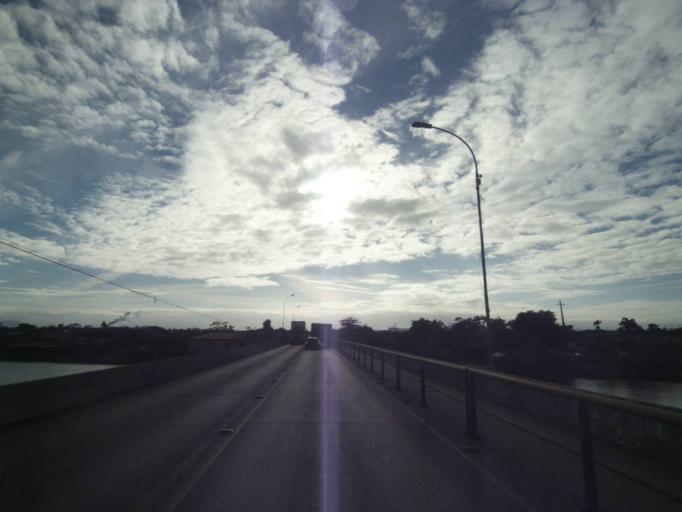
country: BR
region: Parana
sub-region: Paranagua
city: Paranagua
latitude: -25.5211
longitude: -48.5455
